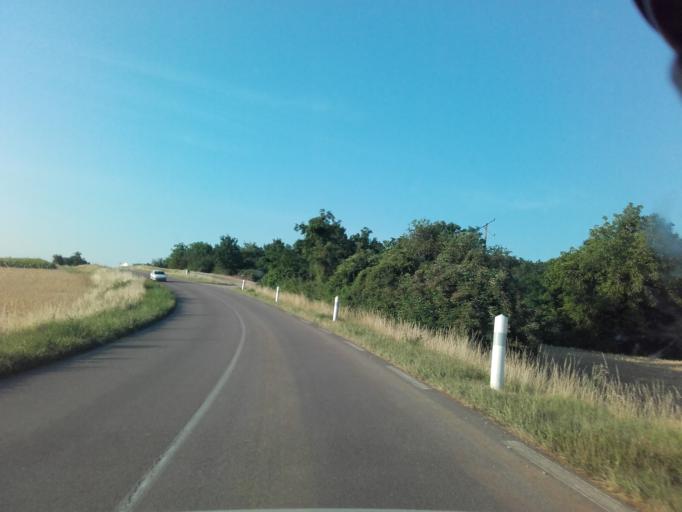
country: FR
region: Bourgogne
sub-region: Departement de Saone-et-Loire
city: Fontaines
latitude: 46.8559
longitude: 4.7525
